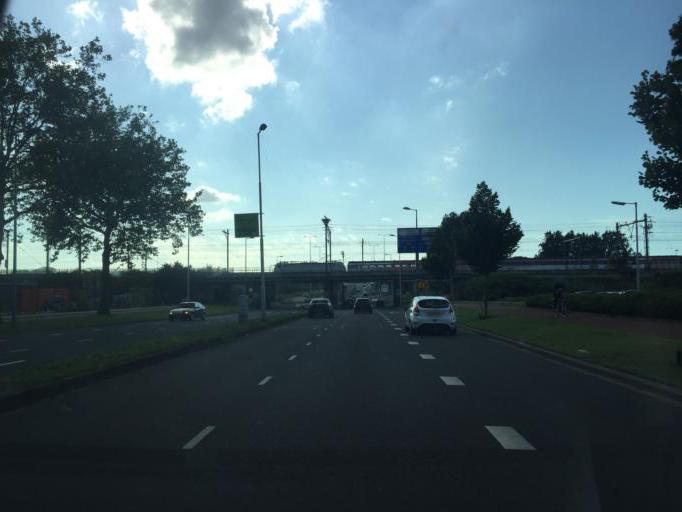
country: NL
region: South Holland
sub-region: Gemeente Rotterdam
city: Delfshaven
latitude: 51.9289
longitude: 4.4507
